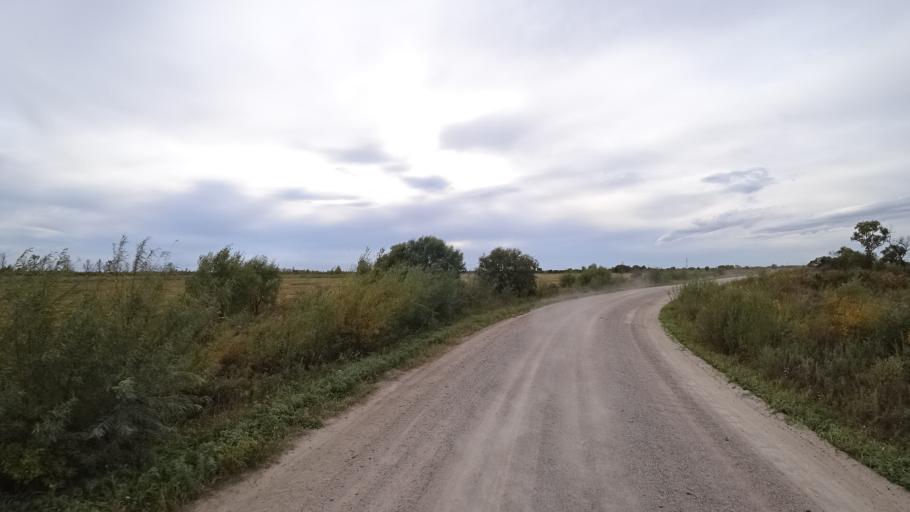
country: RU
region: Amur
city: Arkhara
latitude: 49.3745
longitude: 130.1588
